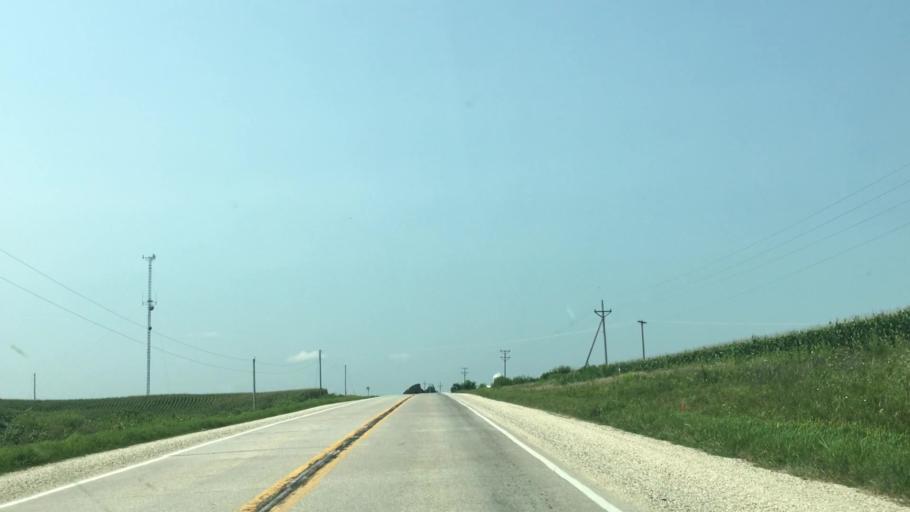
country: US
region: Iowa
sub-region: Fayette County
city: West Union
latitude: 43.0884
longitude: -91.8514
